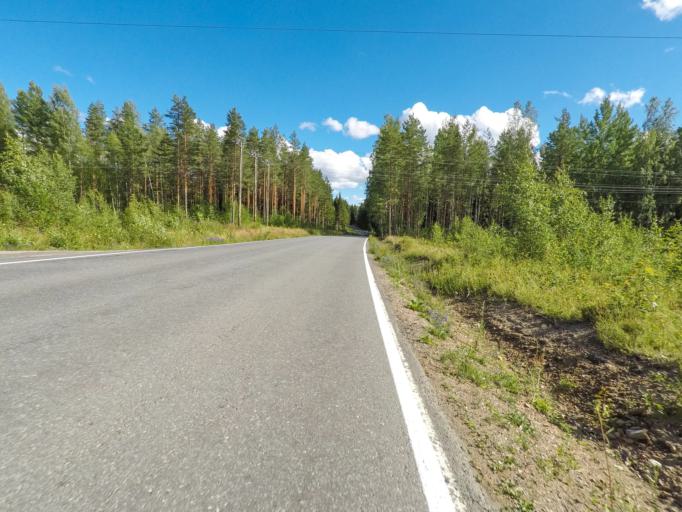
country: FI
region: South Karelia
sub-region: Lappeenranta
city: Taipalsaari
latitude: 61.1759
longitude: 28.0136
